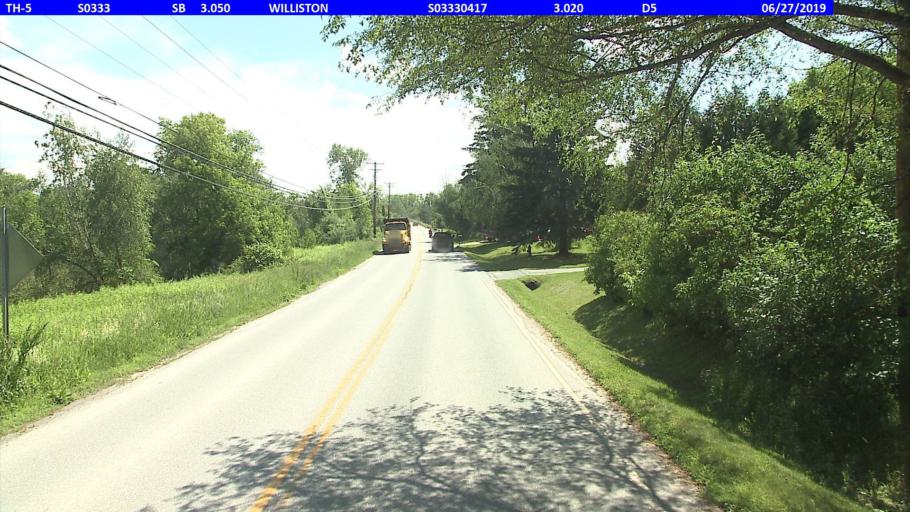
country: US
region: Vermont
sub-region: Chittenden County
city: South Burlington
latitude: 44.4442
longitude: -73.1297
